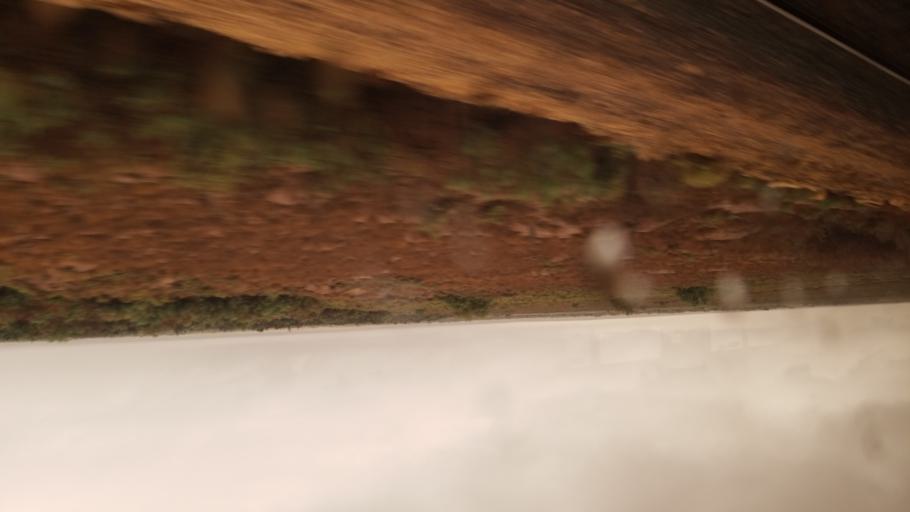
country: US
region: Arizona
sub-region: Navajo County
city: Winslow
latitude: 35.0021
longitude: -110.6387
